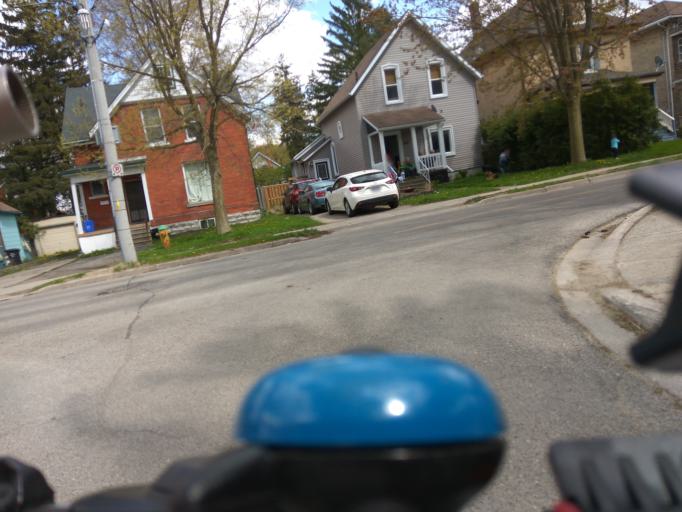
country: CA
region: Ontario
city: Stratford
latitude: 43.3681
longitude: -80.9737
